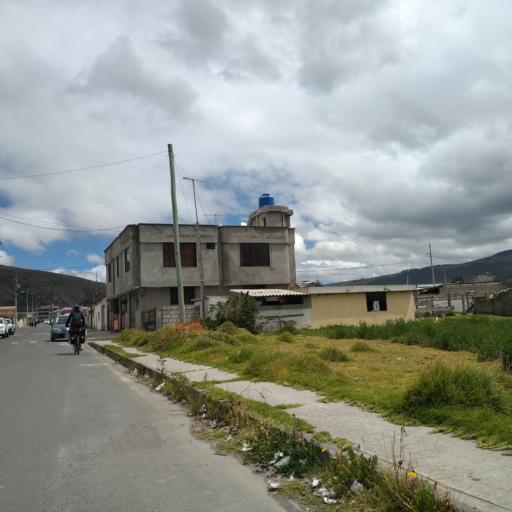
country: EC
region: Cotopaxi
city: Saquisili
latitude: -0.7568
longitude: -78.6829
